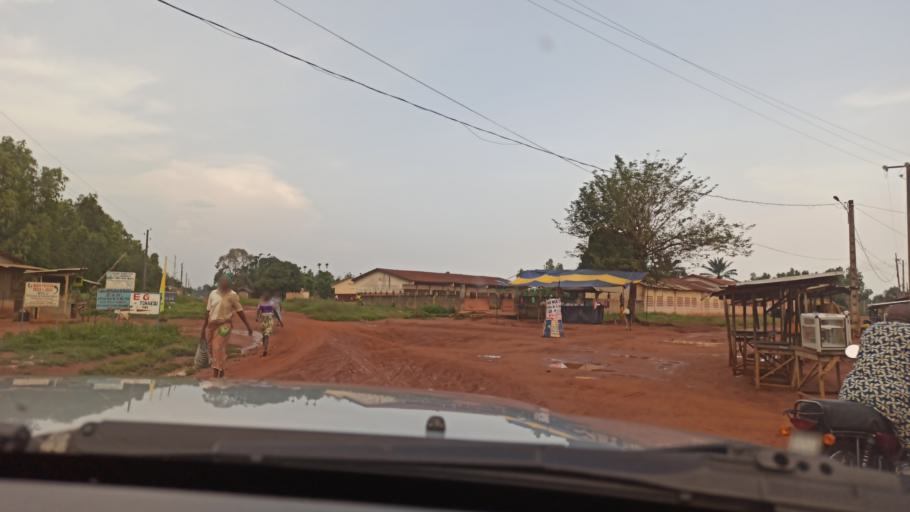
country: BJ
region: Queme
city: Porto-Novo
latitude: 6.4935
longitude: 2.6889
